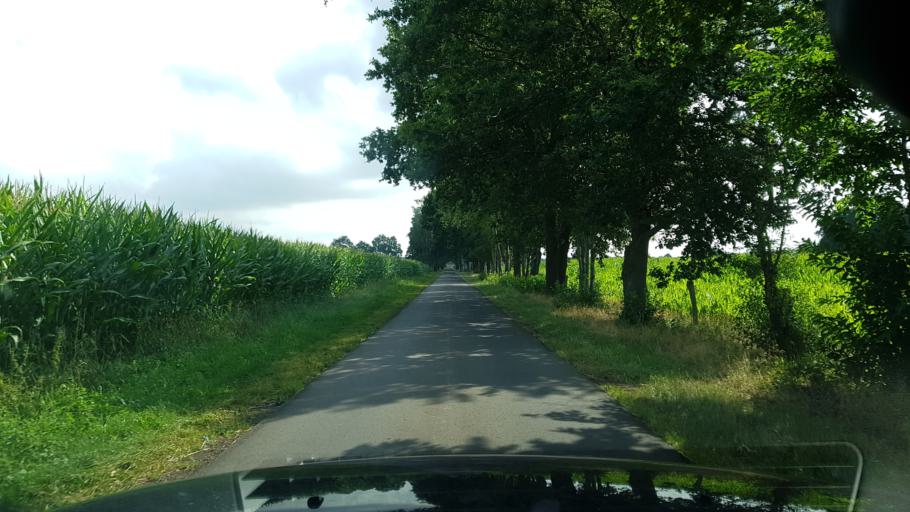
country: DE
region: Lower Saxony
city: Varrel
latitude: 52.6756
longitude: 8.7317
